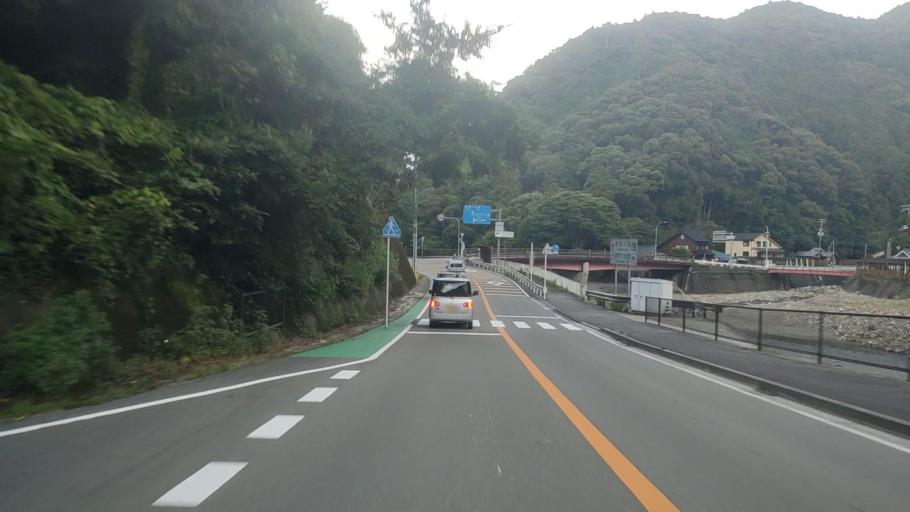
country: JP
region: Wakayama
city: Tanabe
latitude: 33.7748
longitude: 135.5027
